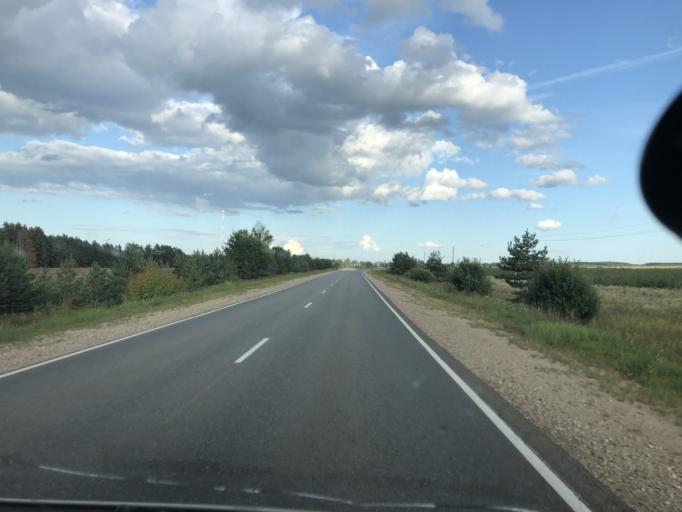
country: RU
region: Kaluga
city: Yukhnov
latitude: 54.7087
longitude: 35.2597
